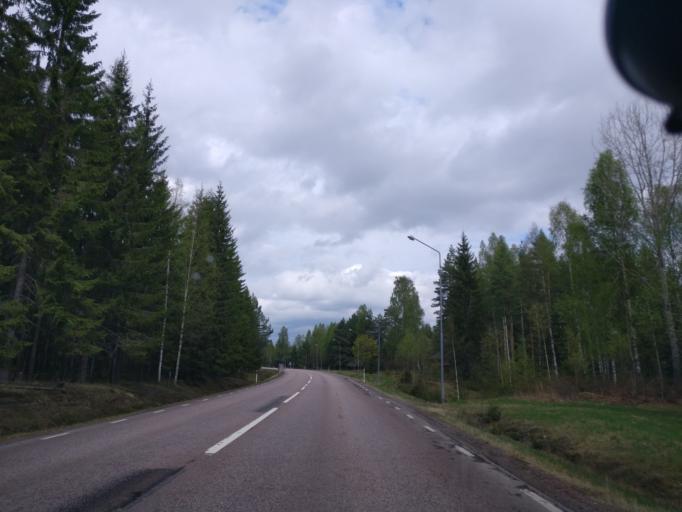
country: SE
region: Vaermland
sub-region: Hagfors Kommun
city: Ekshaerad
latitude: 60.1412
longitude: 13.5251
